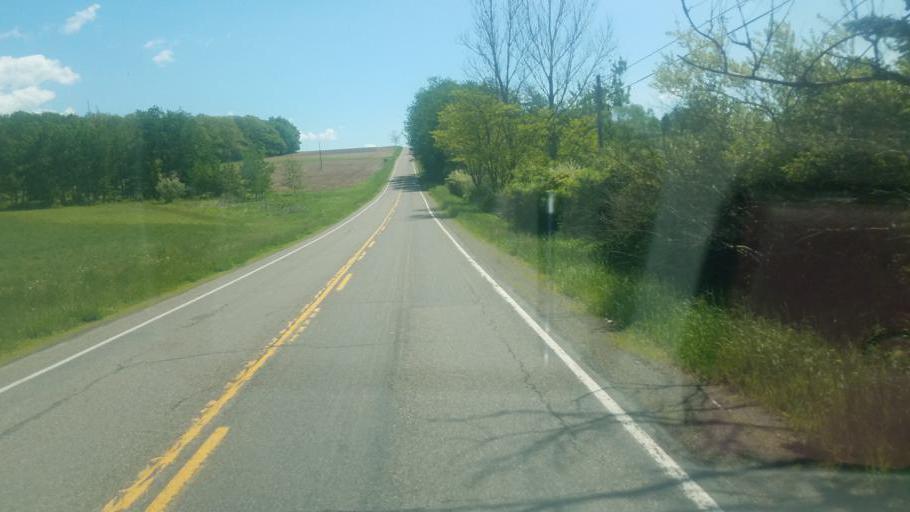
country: US
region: Pennsylvania
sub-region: Tioga County
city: Wellsboro
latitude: 41.7336
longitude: -77.3711
